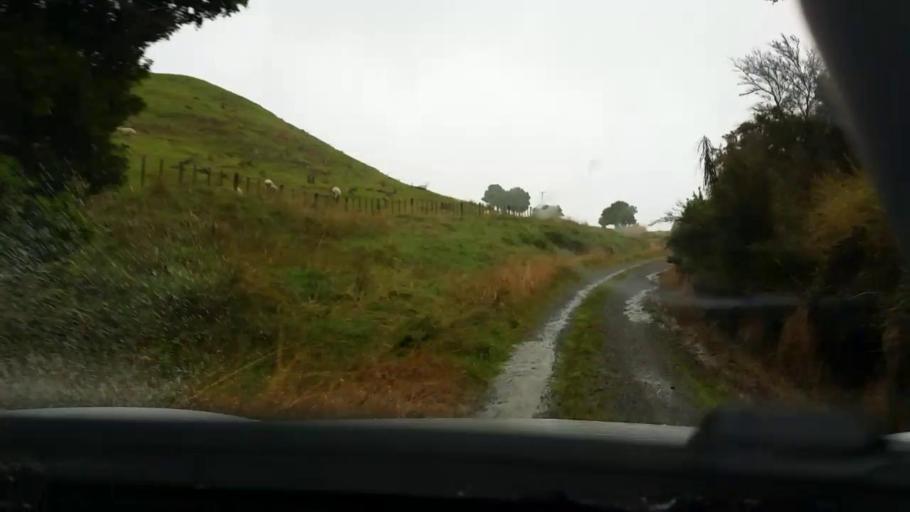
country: NZ
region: Wellington
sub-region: Masterton District
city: Masterton
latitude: -41.1591
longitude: 175.7922
